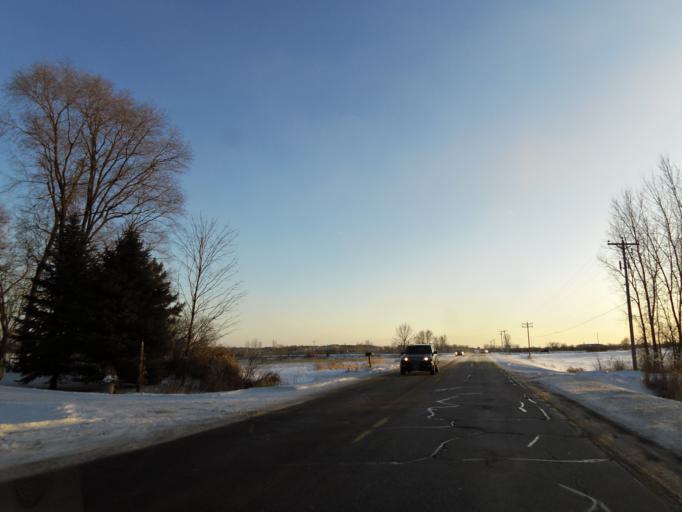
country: US
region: Minnesota
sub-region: Washington County
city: Lake Elmo
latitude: 44.9530
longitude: -92.8831
